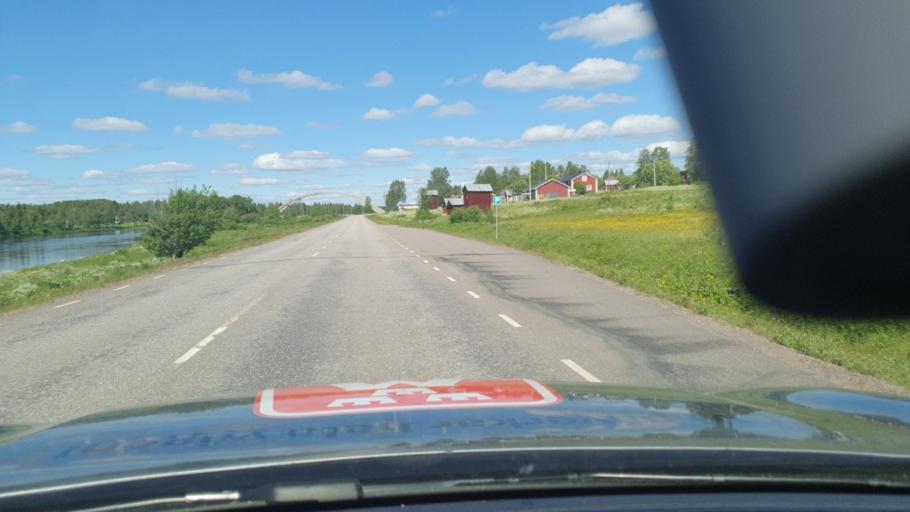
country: SE
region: Norrbotten
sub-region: Pajala Kommun
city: Pajala
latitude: 67.1638
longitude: 22.6221
